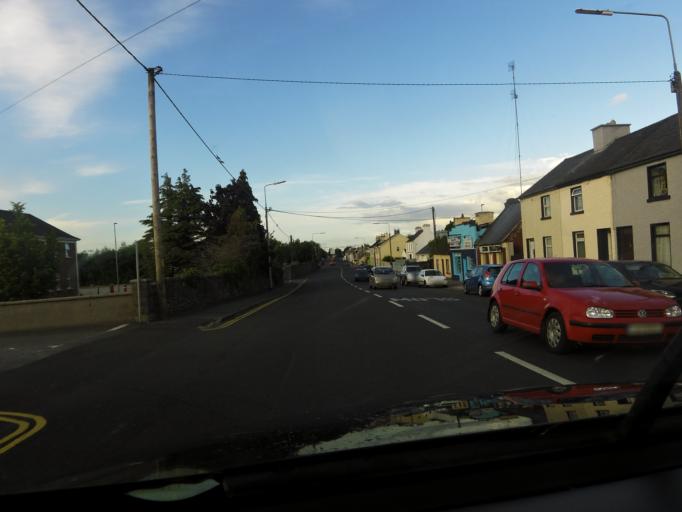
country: IE
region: Connaught
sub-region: County Galway
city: Ballinasloe
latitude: 53.3269
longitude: -8.2331
